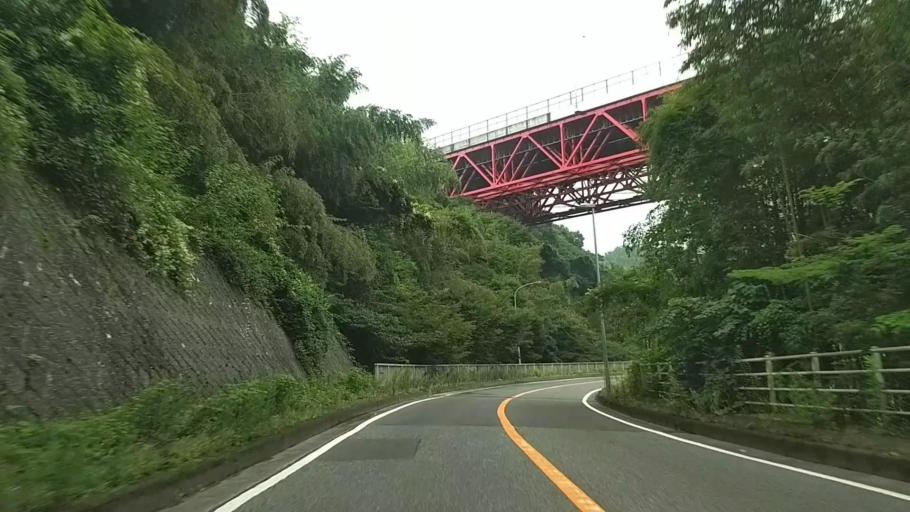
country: JP
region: Kanagawa
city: Hadano
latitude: 35.3397
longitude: 139.1950
